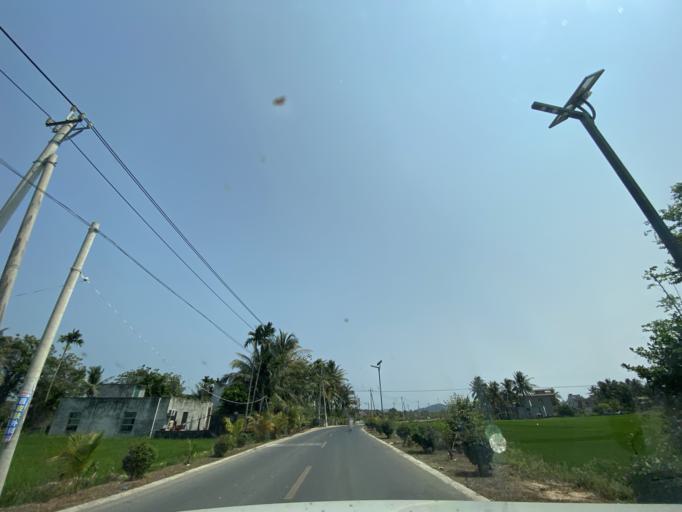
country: CN
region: Hainan
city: Yingzhou
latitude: 18.4187
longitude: 109.8135
